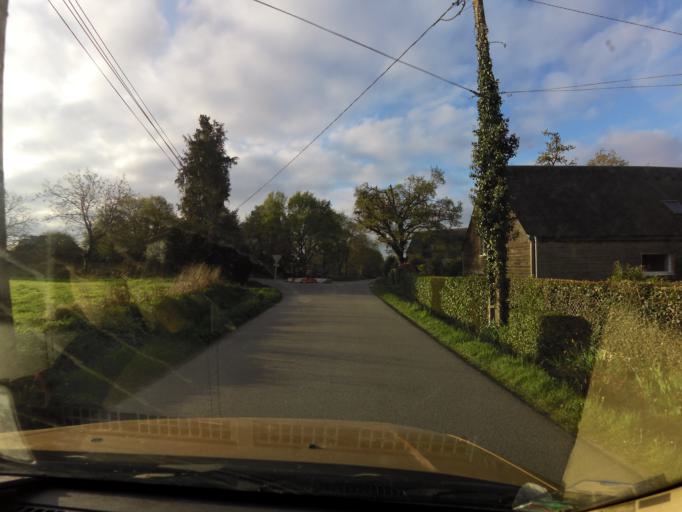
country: FR
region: Brittany
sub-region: Departement du Morbihan
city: Arradon
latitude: 47.6332
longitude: -2.8135
